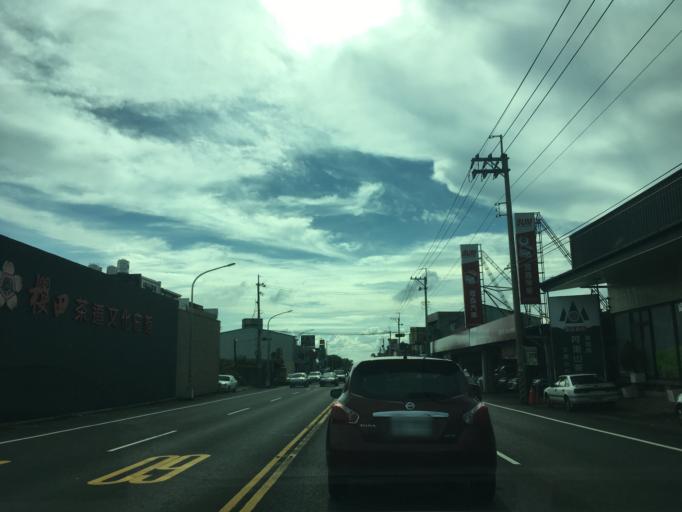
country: TW
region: Taiwan
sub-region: Chiayi
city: Jiayi Shi
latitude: 23.4437
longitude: 120.5080
